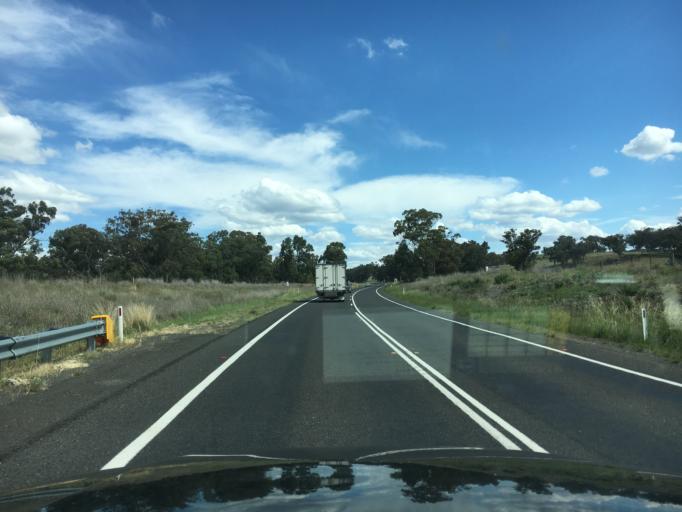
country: AU
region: New South Wales
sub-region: Liverpool Plains
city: Quirindi
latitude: -31.4851
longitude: 150.8642
